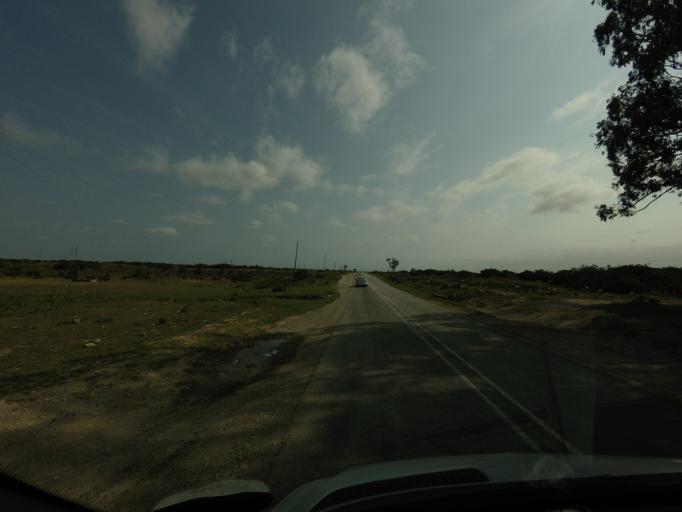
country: ZA
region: Eastern Cape
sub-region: Nelson Mandela Bay Metropolitan Municipality
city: Port Elizabeth
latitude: -33.7702
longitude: 25.5919
